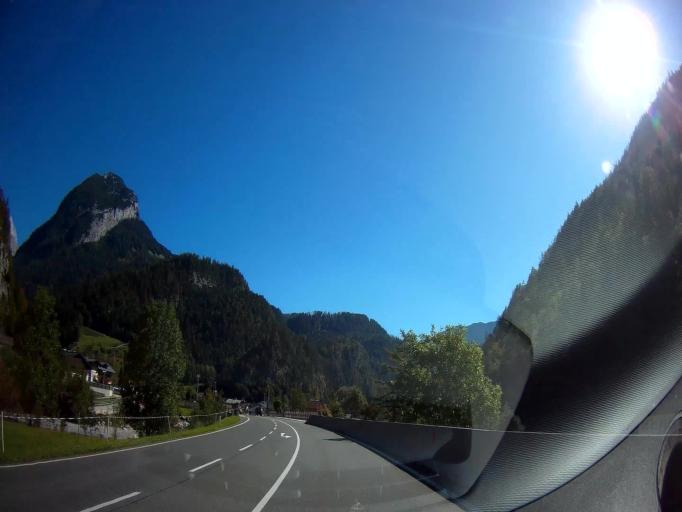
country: AT
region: Salzburg
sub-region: Politischer Bezirk Zell am See
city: Sankt Martin bei Lofer
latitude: 47.5217
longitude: 12.7481
